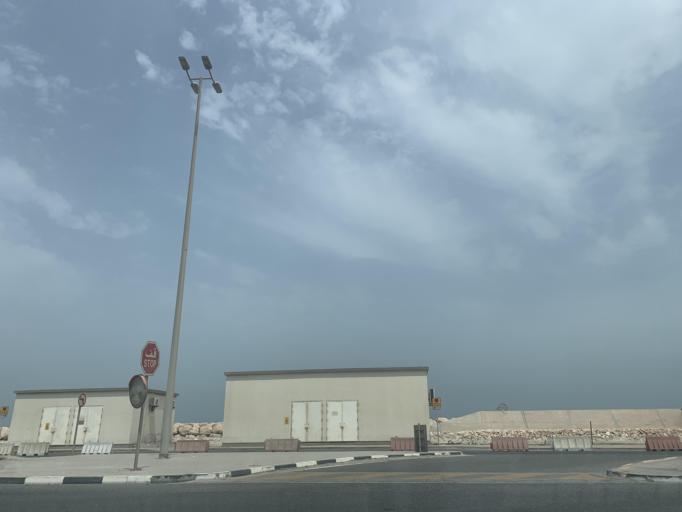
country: BH
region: Muharraq
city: Al Hadd
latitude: 26.1981
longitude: 50.7107
